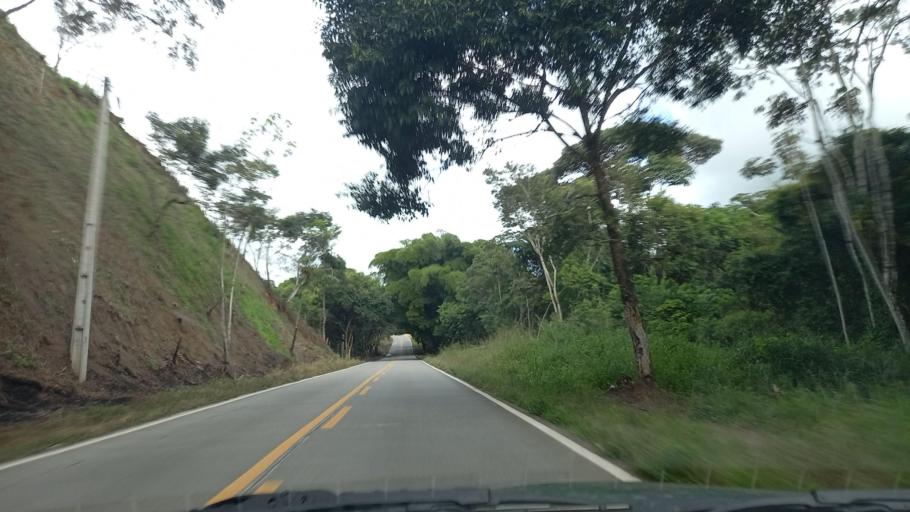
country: BR
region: Pernambuco
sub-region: Maraial
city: Maraial
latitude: -8.7845
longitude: -35.9078
